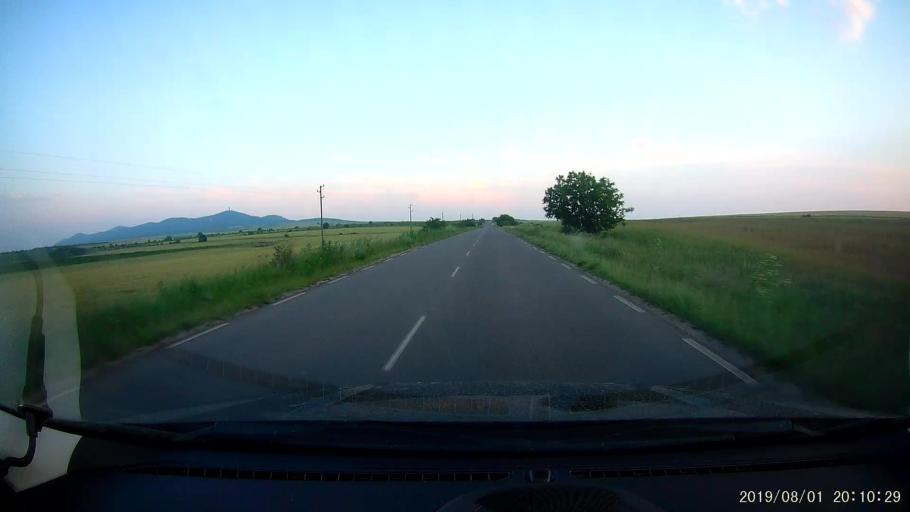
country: BG
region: Yambol
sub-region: Obshtina Yambol
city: Yambol
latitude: 42.4804
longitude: 26.5997
